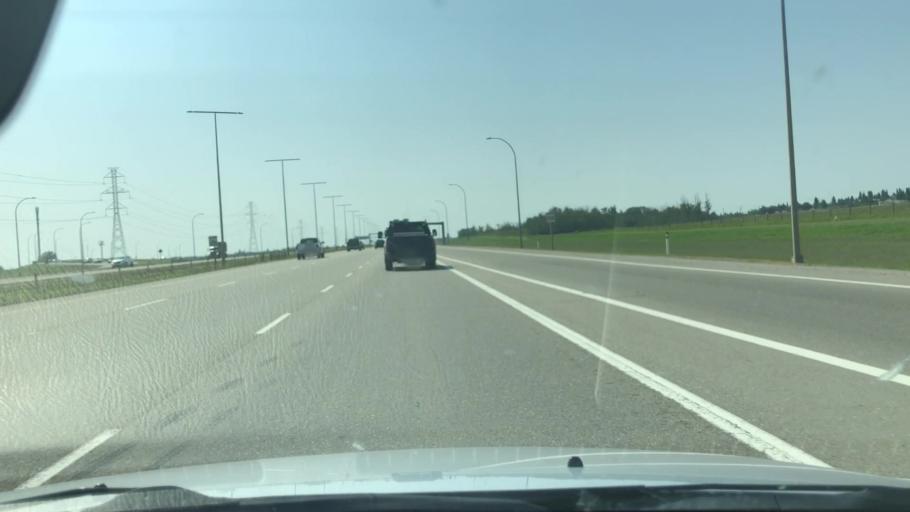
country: CA
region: Alberta
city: St. Albert
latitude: 53.5223
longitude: -113.6595
